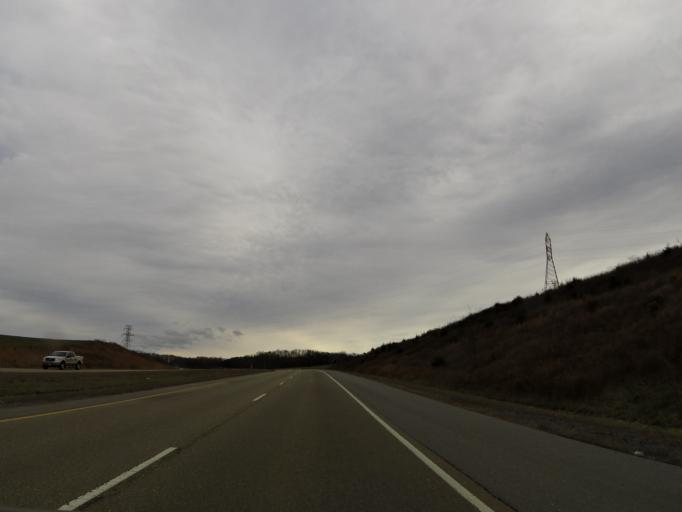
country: US
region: Tennessee
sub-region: Cocke County
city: Newport
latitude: 36.0051
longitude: -83.0766
